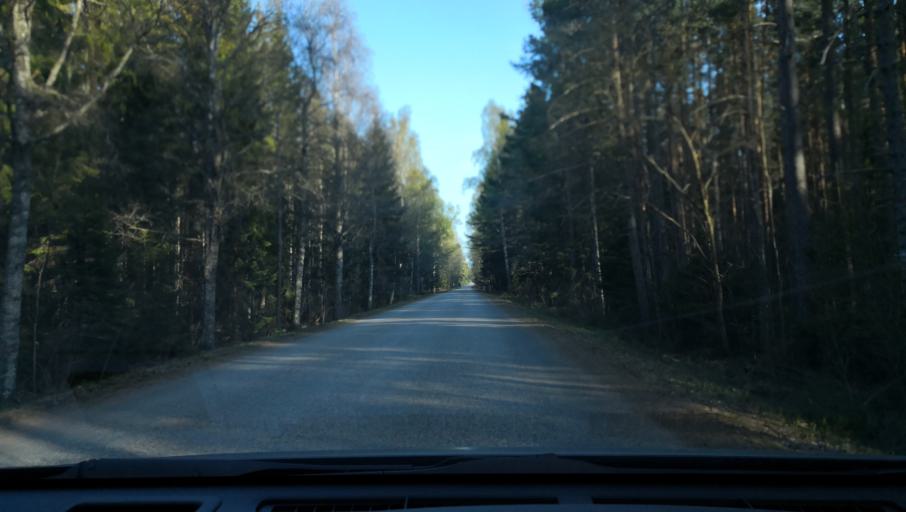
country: SE
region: Uppsala
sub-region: Heby Kommun
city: Tarnsjo
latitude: 60.2732
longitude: 16.9024
